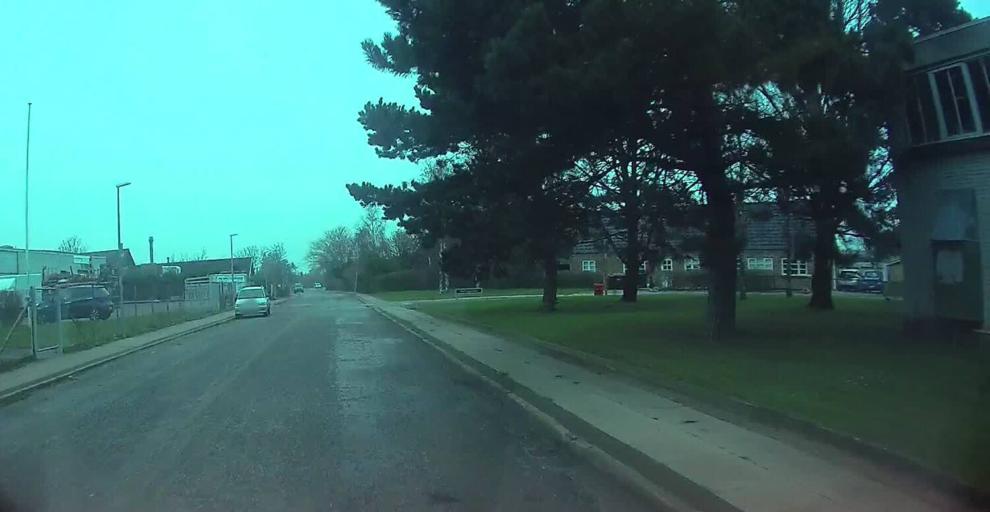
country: DK
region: Capital Region
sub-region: Tarnby Kommune
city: Tarnby
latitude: 55.6259
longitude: 12.5983
